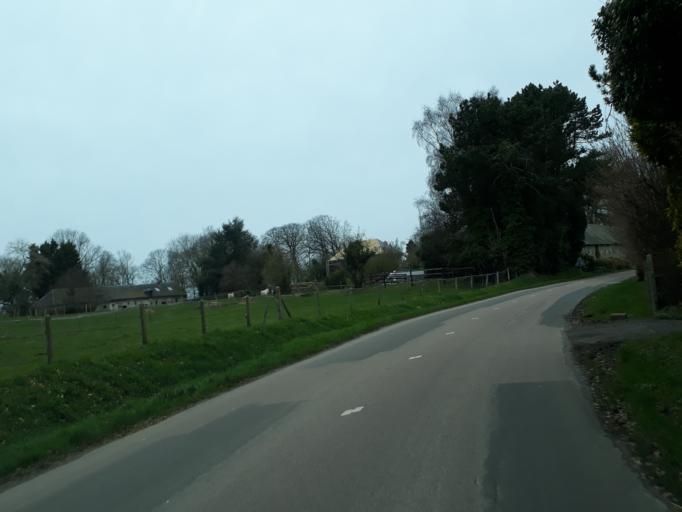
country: FR
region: Haute-Normandie
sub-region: Departement de la Seine-Maritime
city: Les Loges
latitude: 49.7181
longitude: 0.2843
